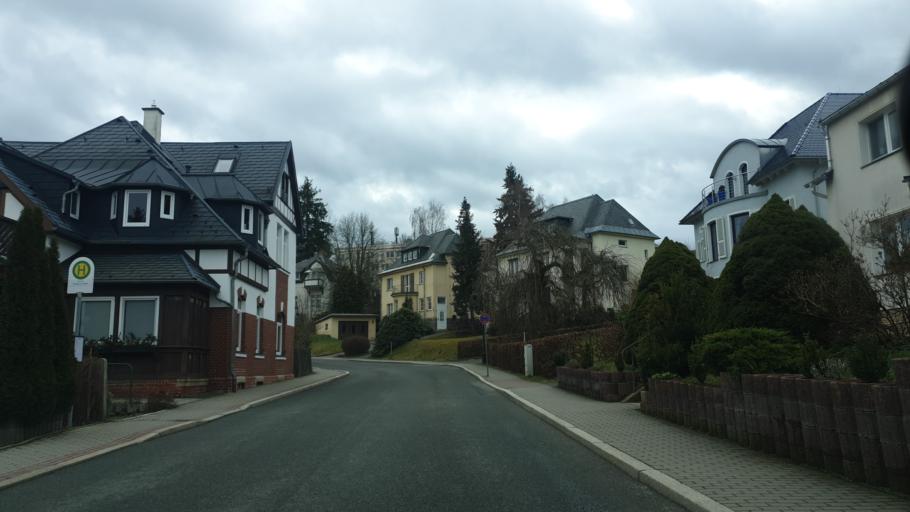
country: DE
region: Saxony
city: Bad Elster
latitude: 50.2832
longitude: 12.2309
